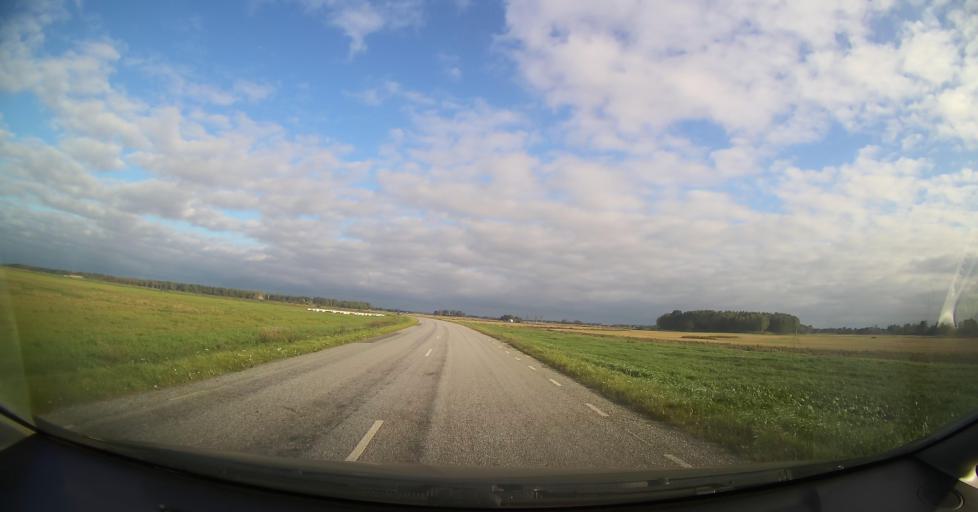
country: EE
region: Harju
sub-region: Raasiku vald
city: Arukula
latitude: 59.4162
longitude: 25.0784
